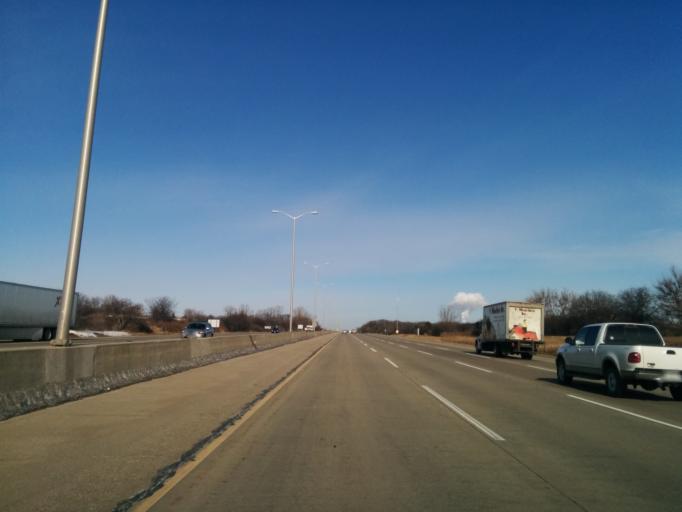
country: US
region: Illinois
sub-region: Lake County
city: Grandwood Park
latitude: 42.3961
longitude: -87.9488
